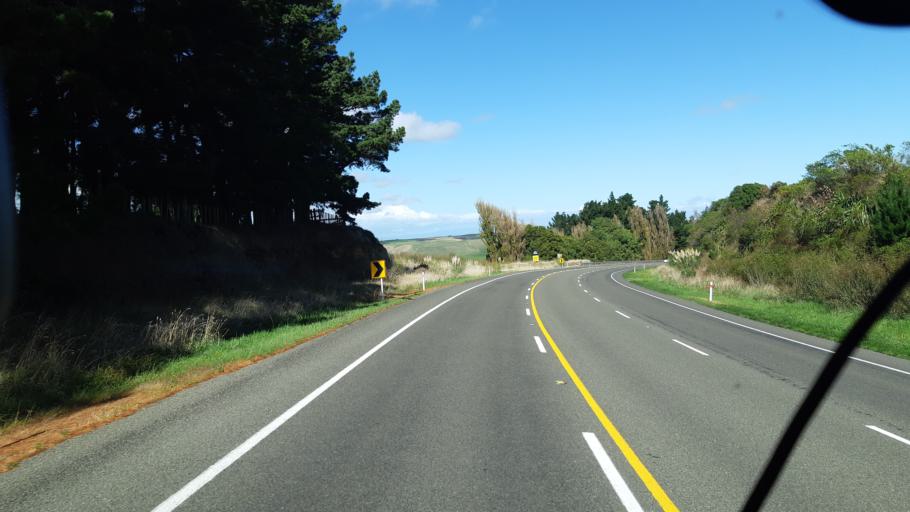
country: NZ
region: Manawatu-Wanganui
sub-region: Wanganui District
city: Wanganui
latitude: -39.9945
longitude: 175.1686
